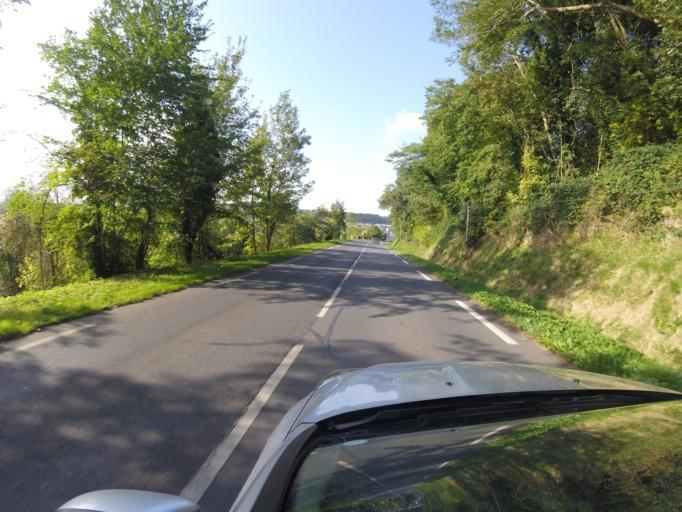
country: FR
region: Haute-Normandie
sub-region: Departement de la Seine-Maritime
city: Fecamp
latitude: 49.7602
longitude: 0.3936
